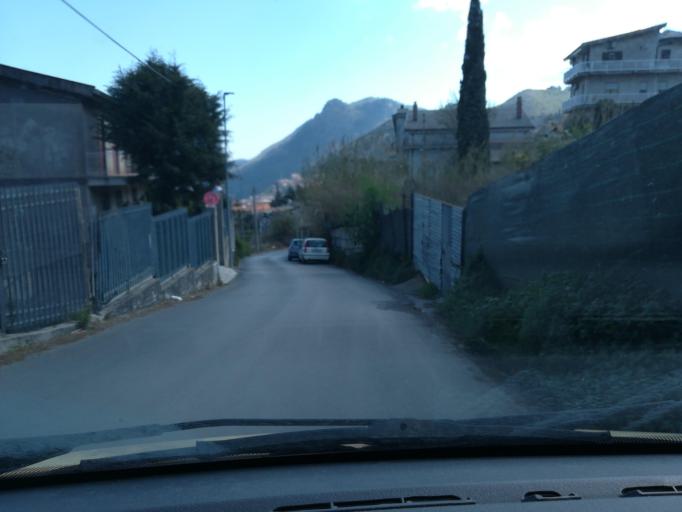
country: IT
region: Sicily
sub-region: Palermo
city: Altofonte
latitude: 38.0412
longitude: 13.2896
